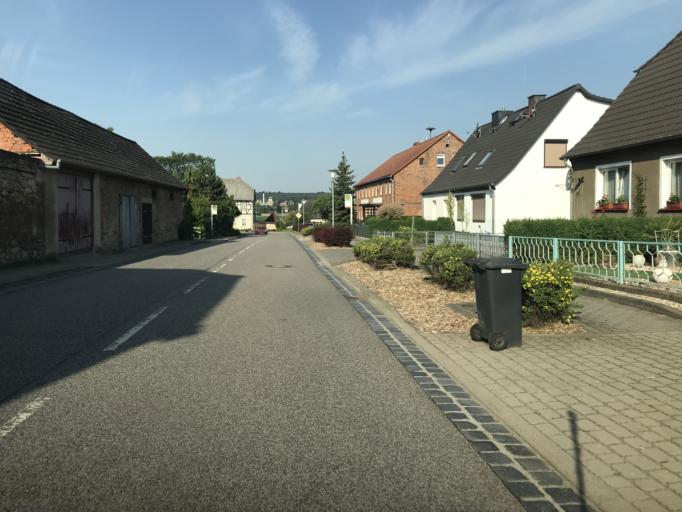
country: DE
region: Saxony-Anhalt
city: Beendorf
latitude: 52.2420
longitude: 11.1083
